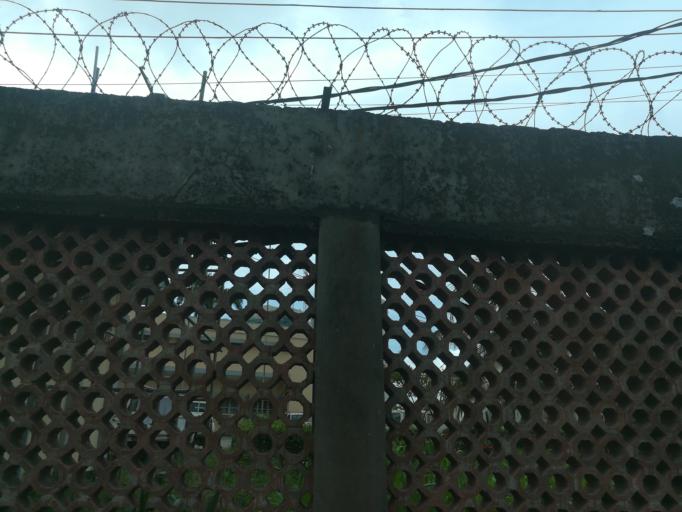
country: NG
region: Lagos
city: Lagos
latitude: 6.4222
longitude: 3.4104
